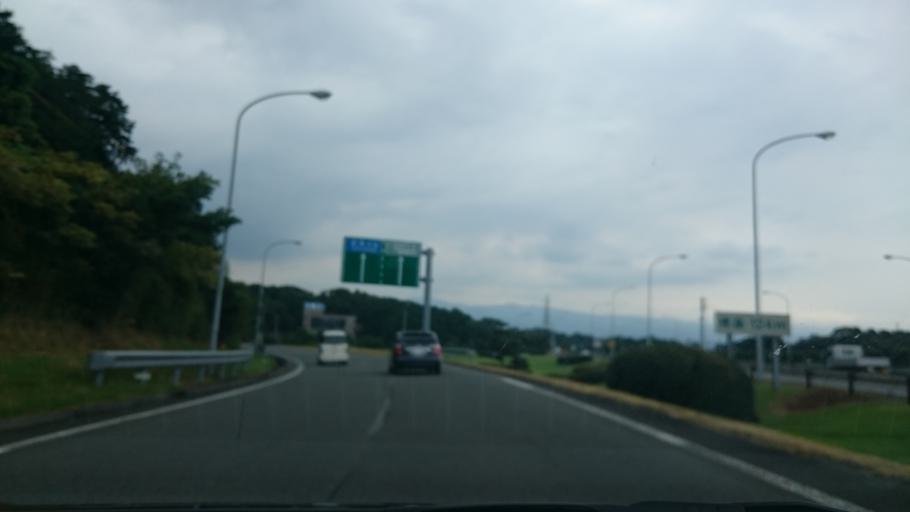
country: JP
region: Shizuoka
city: Numazu
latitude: 35.1468
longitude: 138.8628
